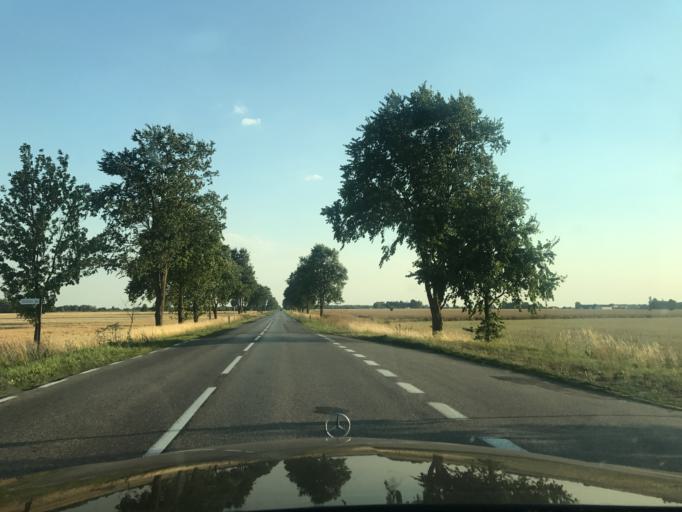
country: PL
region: Lublin Voivodeship
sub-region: Powiat parczewski
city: Jablon
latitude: 51.6864
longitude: 23.0310
